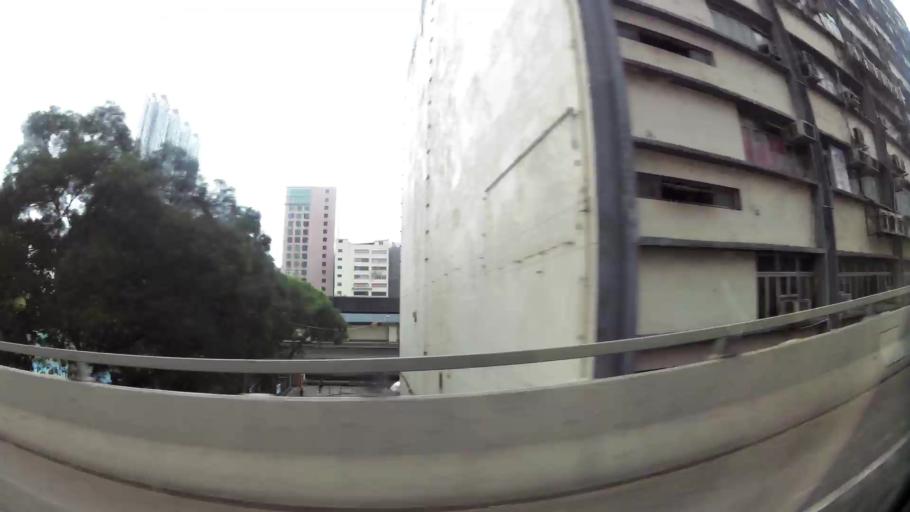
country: HK
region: Kowloon City
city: Kowloon
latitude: 22.3191
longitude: 114.1895
